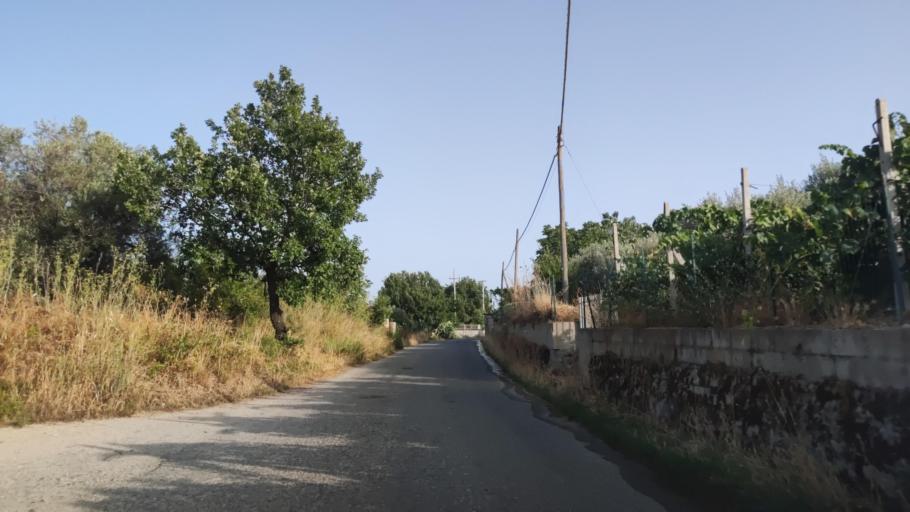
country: IT
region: Calabria
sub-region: Provincia di Reggio Calabria
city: Stignano
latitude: 38.4287
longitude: 16.4620
